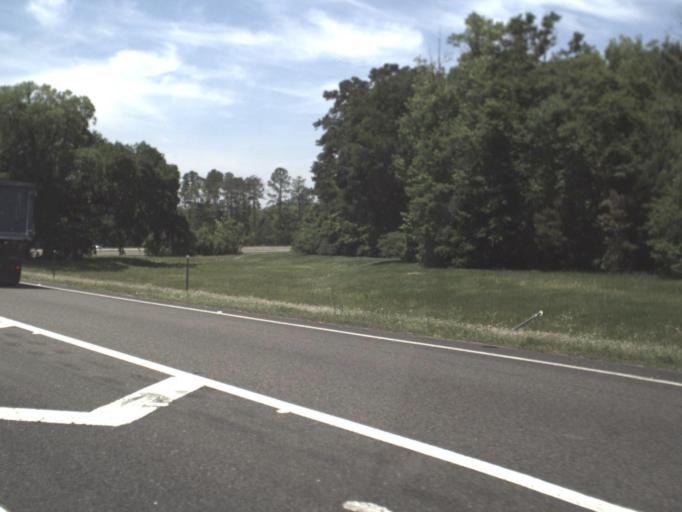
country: US
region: Florida
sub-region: Duval County
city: Jacksonville
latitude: 30.4602
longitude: -81.6754
